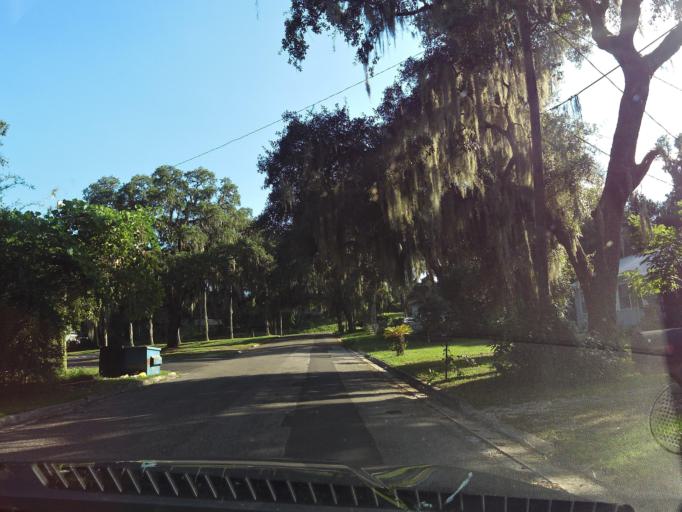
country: US
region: Florida
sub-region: Putnam County
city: Palatka
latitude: 29.6396
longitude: -81.6443
